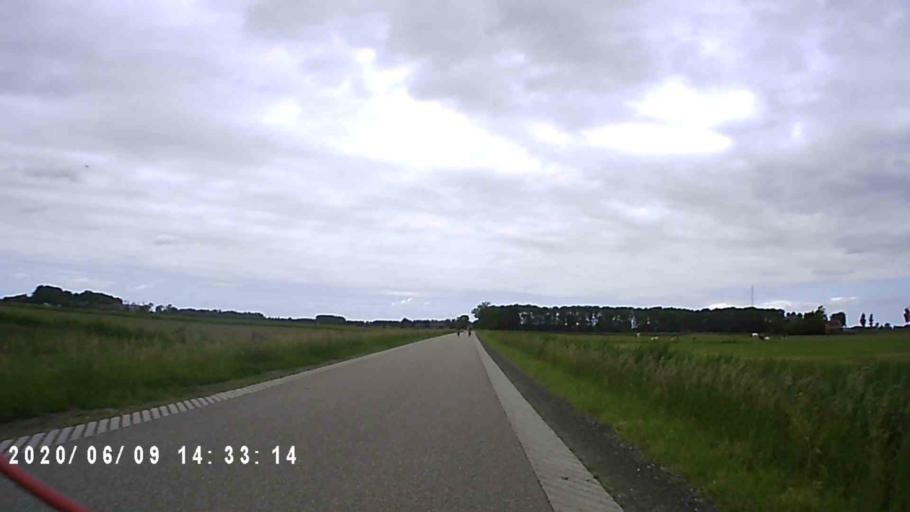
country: NL
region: Groningen
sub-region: Gemeente Bedum
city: Bedum
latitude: 53.3223
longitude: 6.5910
